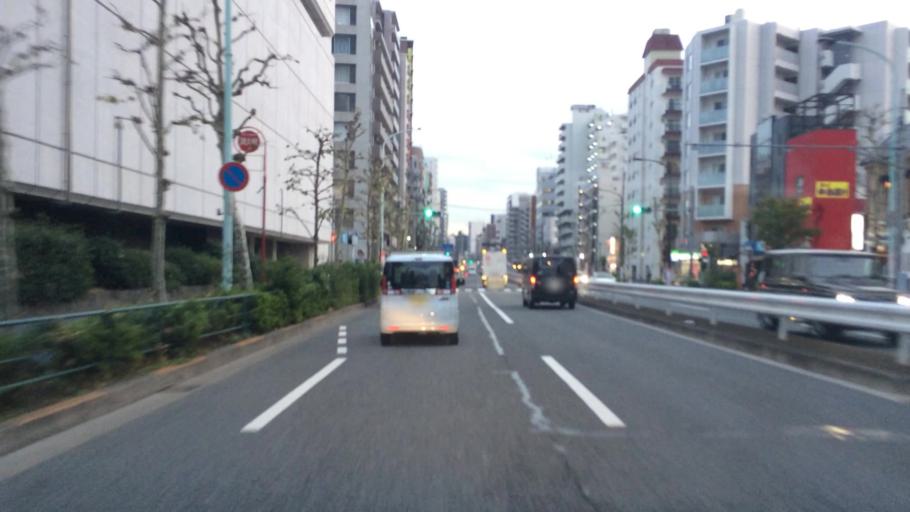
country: JP
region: Tokyo
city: Tokyo
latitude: 35.6354
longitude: 139.7066
